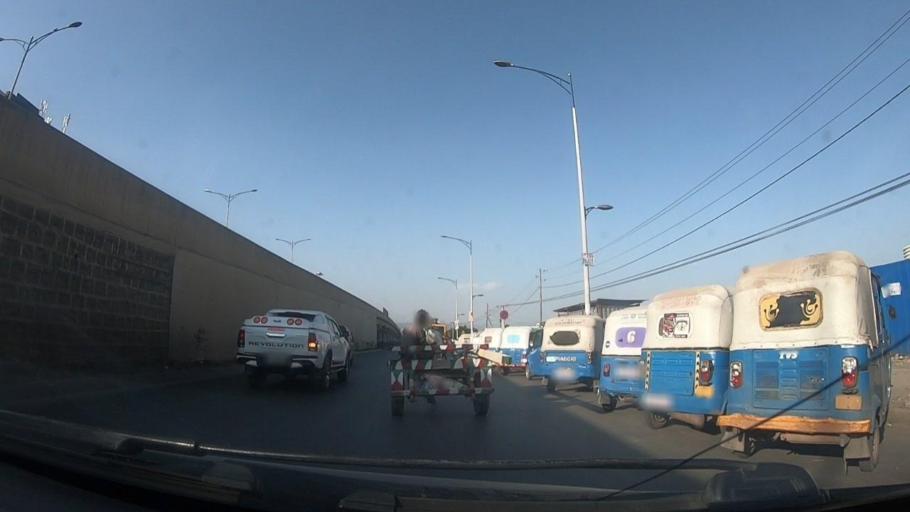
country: ET
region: Adis Abeba
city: Addis Ababa
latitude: 8.9353
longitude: 38.7346
